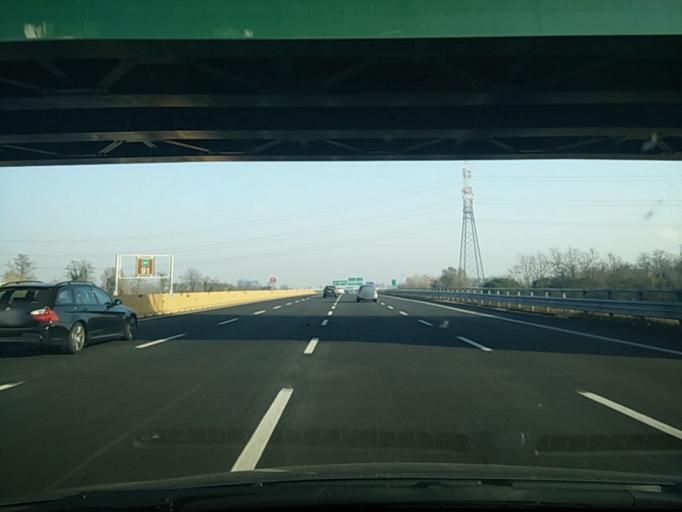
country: IT
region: Lombardy
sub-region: Citta metropolitana di Milano
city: Vighignolo
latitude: 45.5108
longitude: 9.0479
